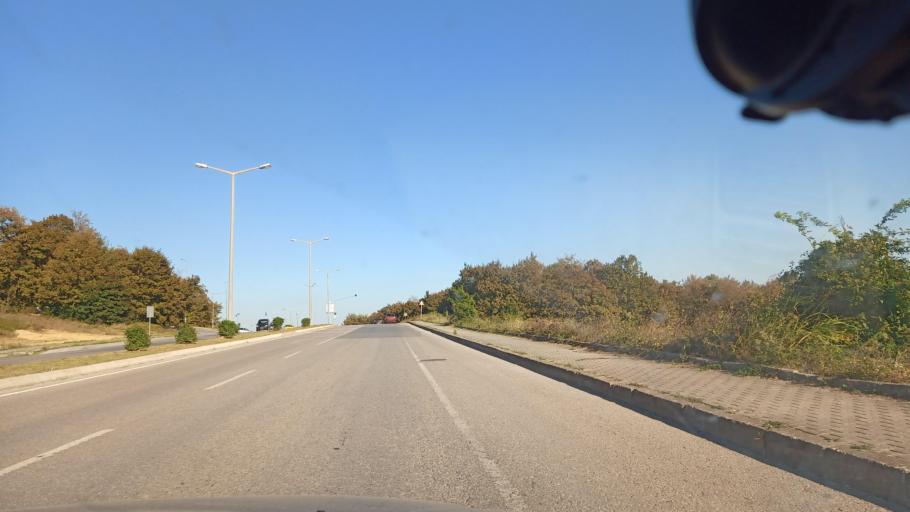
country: TR
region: Sakarya
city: Kazimpasa
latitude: 40.8539
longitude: 30.2914
